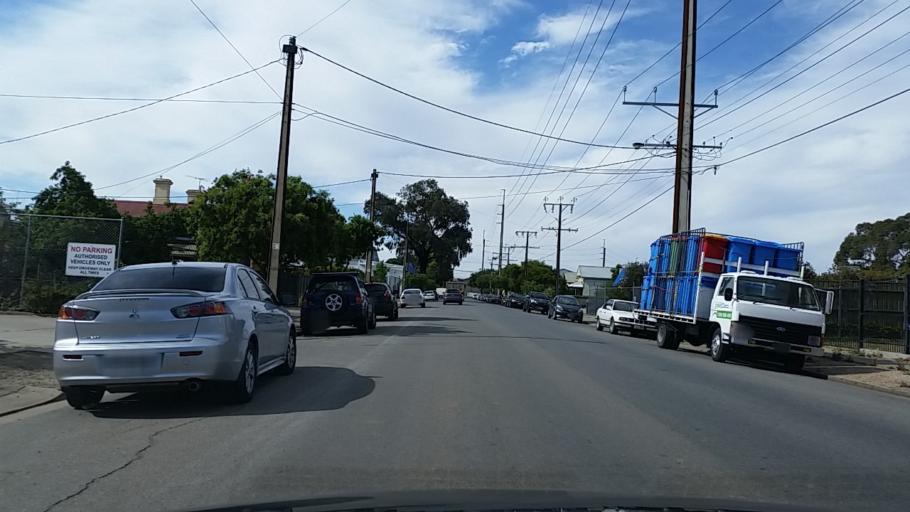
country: AU
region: South Australia
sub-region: City of West Torrens
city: Thebarton
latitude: -34.9075
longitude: 138.5666
